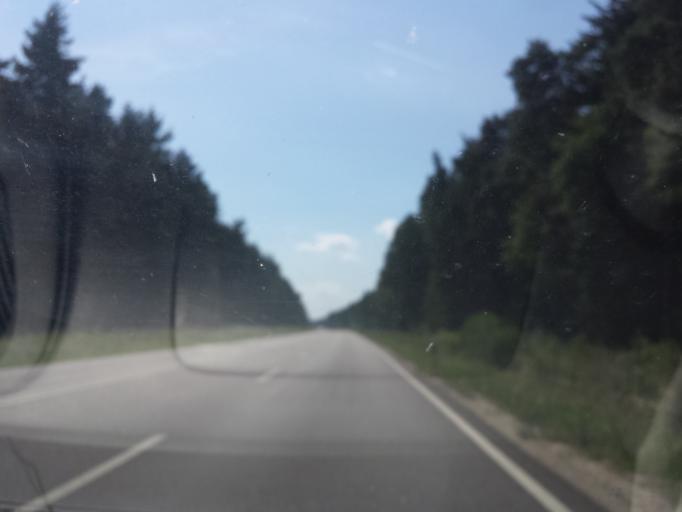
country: DE
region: Bavaria
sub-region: Lower Bavaria
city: Neustadt an der Donau
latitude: 48.7773
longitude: 11.7605
